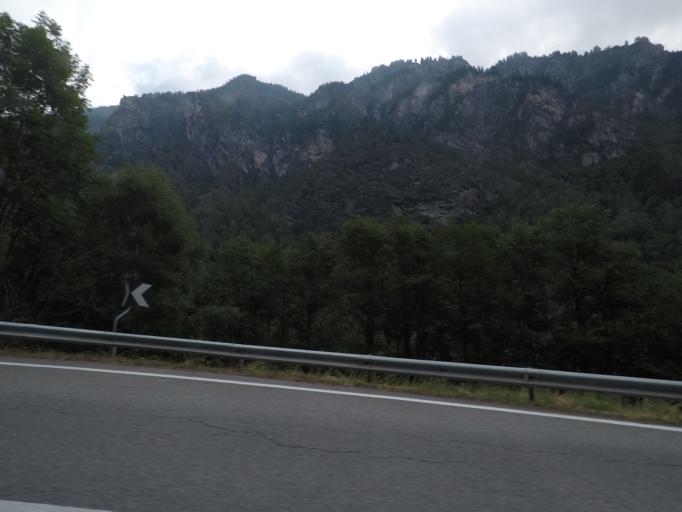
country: IT
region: Aosta Valley
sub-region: Valle d'Aosta
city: Chamois
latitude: 45.8417
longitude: 7.6048
